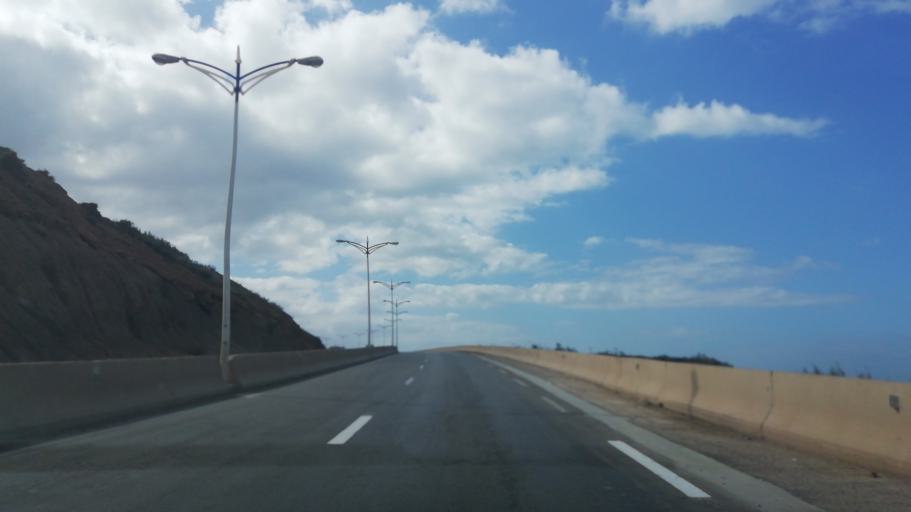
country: DZ
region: Mostaganem
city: Mostaganem
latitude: 36.0101
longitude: 0.1273
